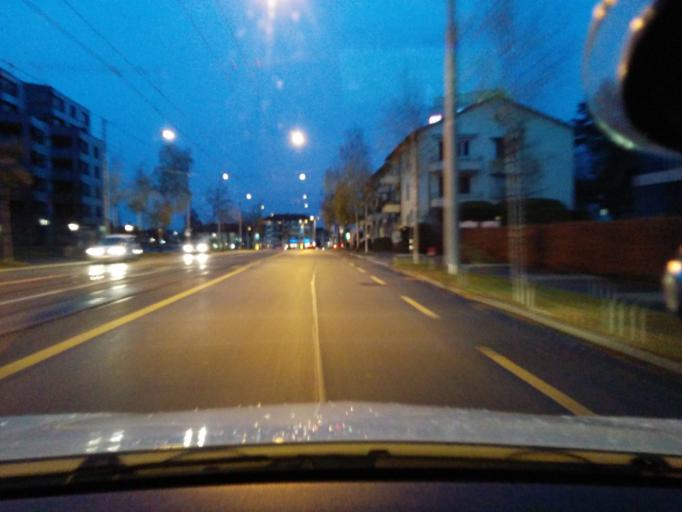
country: CH
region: Zurich
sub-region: Bezirk Zuerich
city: Zuerich (Kreis 6) / Unterstrass
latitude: 47.4003
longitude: 8.5339
